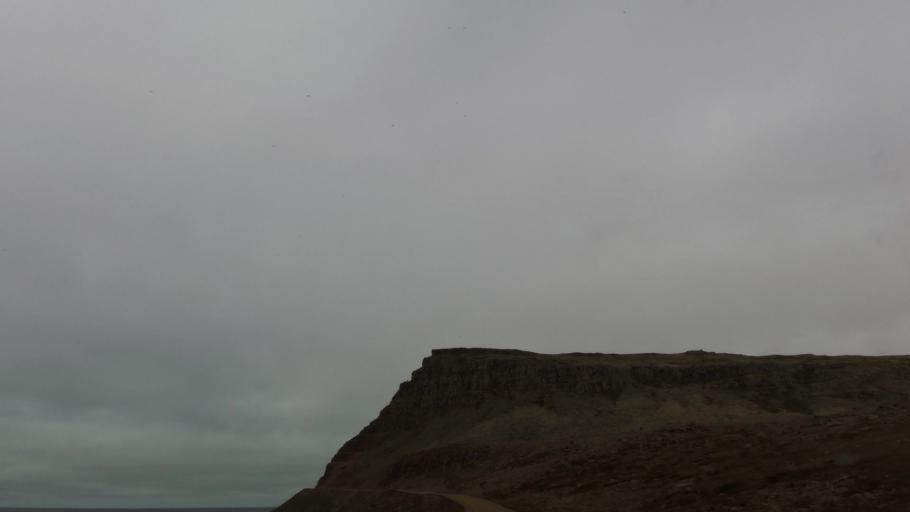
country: IS
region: West
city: Olafsvik
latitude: 65.5069
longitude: -24.5150
